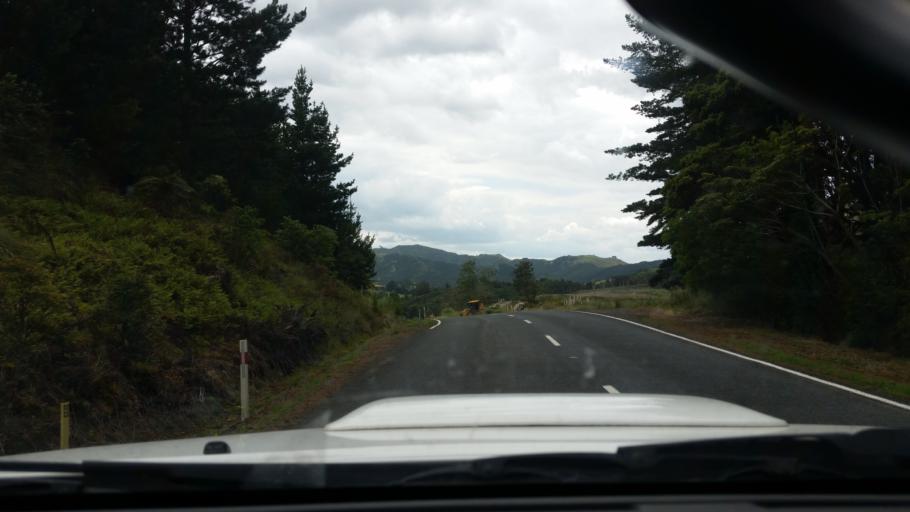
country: NZ
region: Northland
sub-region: Kaipara District
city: Dargaville
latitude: -35.7252
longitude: 173.8598
